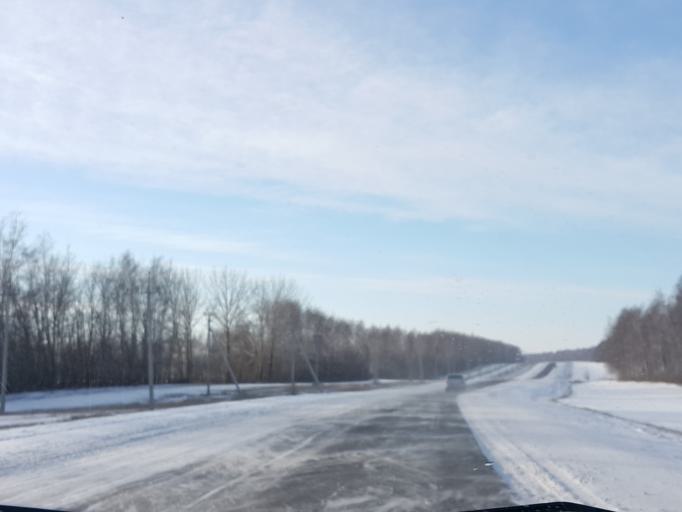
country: RU
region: Tambov
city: Znamenka
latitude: 52.3828
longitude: 41.3311
